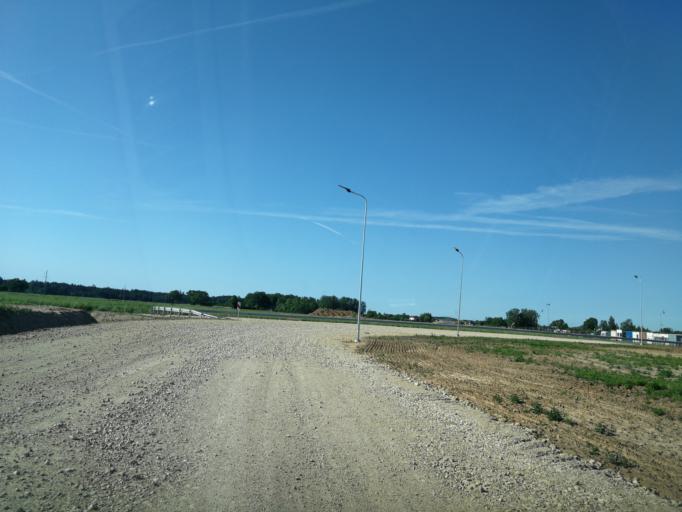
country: LV
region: Adazi
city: Adazi
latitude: 57.0951
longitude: 24.3039
